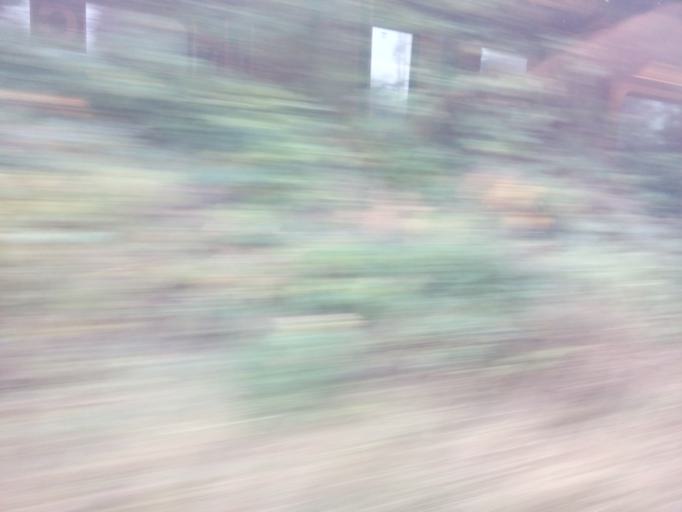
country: GB
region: England
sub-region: City and Borough of Leeds
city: Scholes
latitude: 53.8052
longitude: -1.4481
